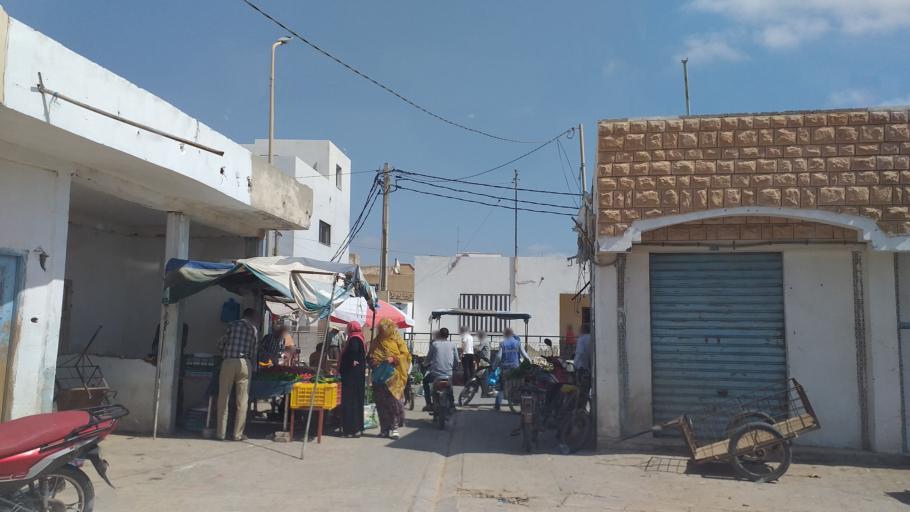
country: TN
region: Qabis
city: Gabes
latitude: 33.9398
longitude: 10.0661
